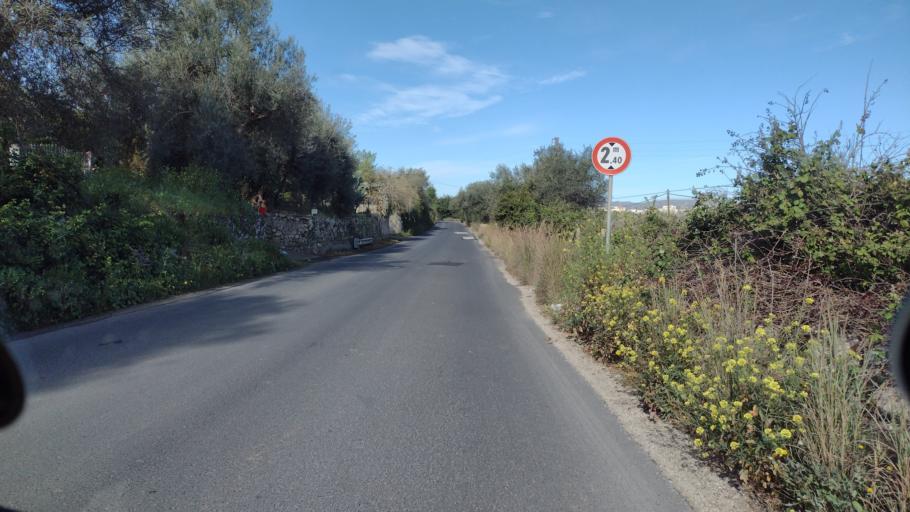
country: IT
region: Sicily
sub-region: Provincia di Siracusa
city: Noto
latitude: 36.8770
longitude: 15.0968
